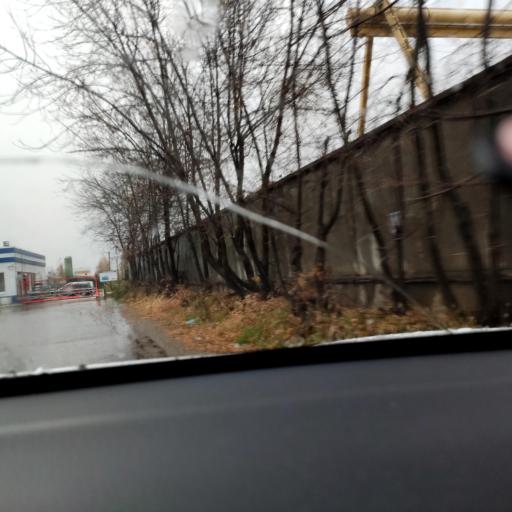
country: RU
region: Tatarstan
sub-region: Gorod Kazan'
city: Kazan
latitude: 55.8674
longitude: 49.1099
